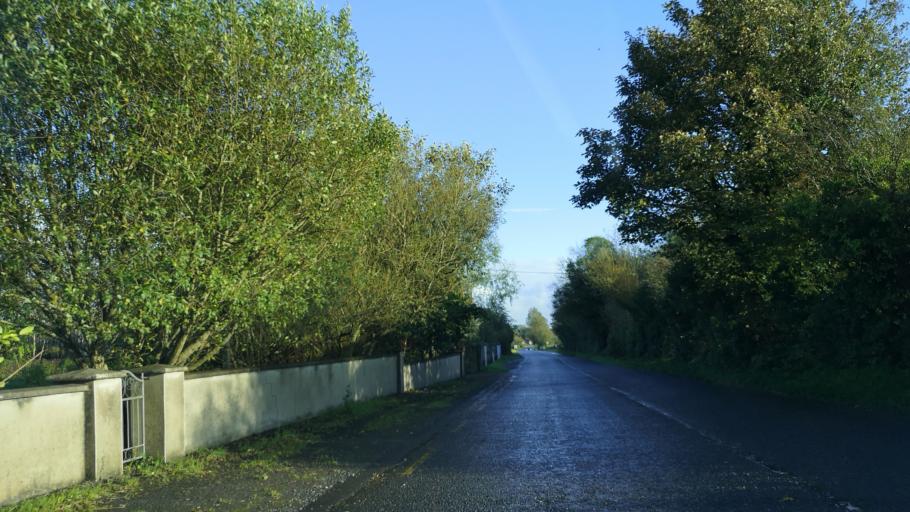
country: IE
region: Connaught
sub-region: Roscommon
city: Castlerea
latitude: 53.7865
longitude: -8.4907
